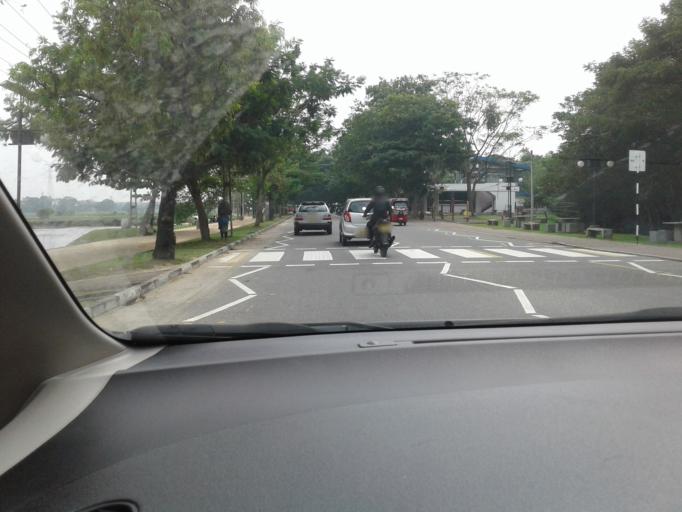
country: LK
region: Western
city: Sri Jayewardenepura Kotte
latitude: 6.8765
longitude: 79.9270
